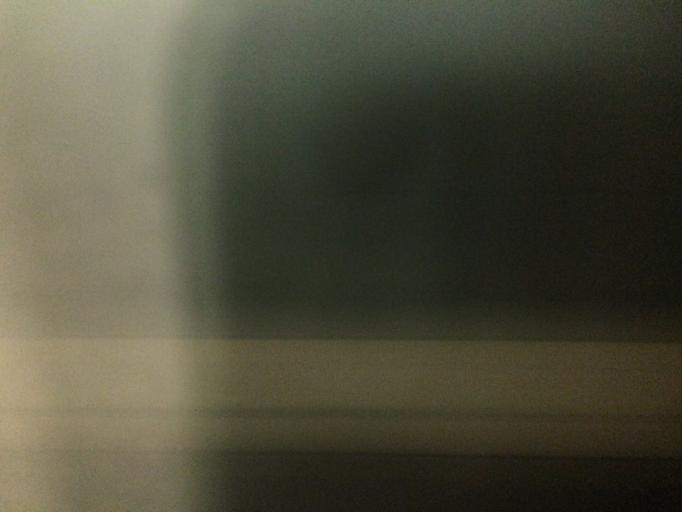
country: TW
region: Taiwan
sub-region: Miaoli
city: Miaoli
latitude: 24.5287
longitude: 120.7397
